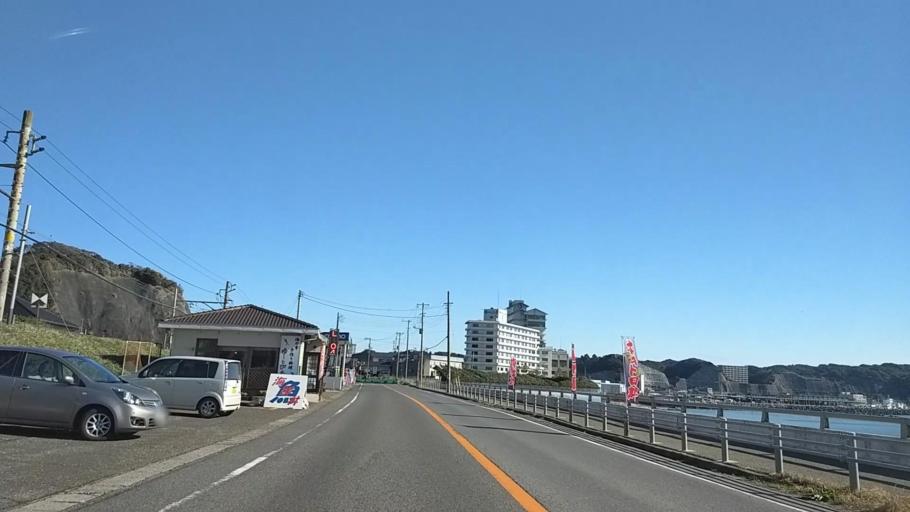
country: JP
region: Chiba
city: Katsuura
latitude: 35.1512
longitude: 140.3054
